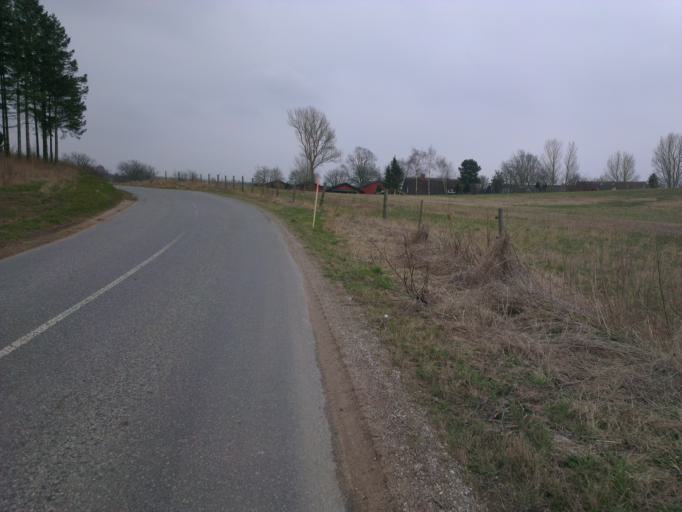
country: DK
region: Capital Region
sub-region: Egedal Kommune
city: Olstykke
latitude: 55.8337
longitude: 12.1294
